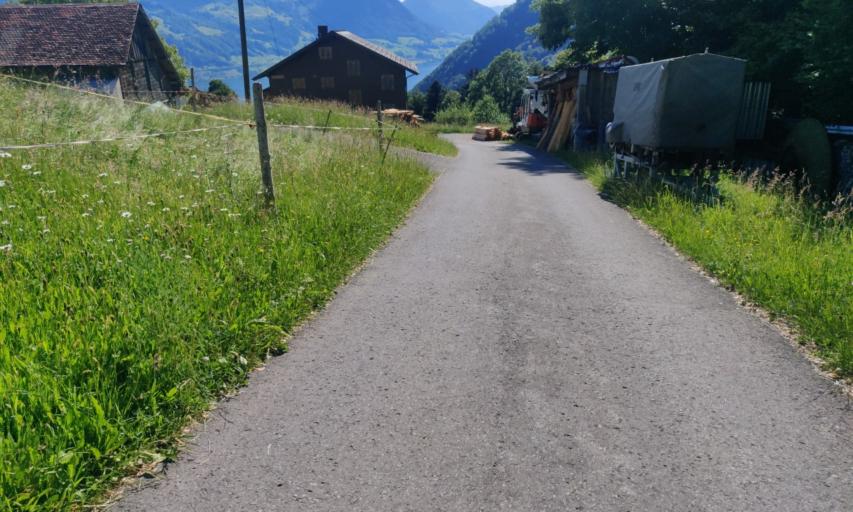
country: CH
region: Schwyz
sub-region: Bezirk Gersau
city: Gersau
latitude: 47.0050
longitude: 8.5362
